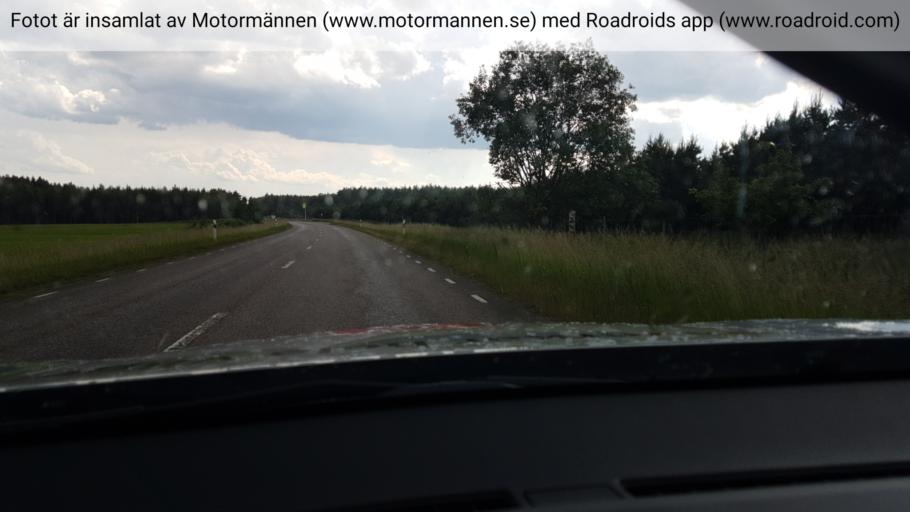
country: SE
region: Vaestra Goetaland
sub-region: Hjo Kommun
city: Hjo
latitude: 58.2518
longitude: 14.2344
